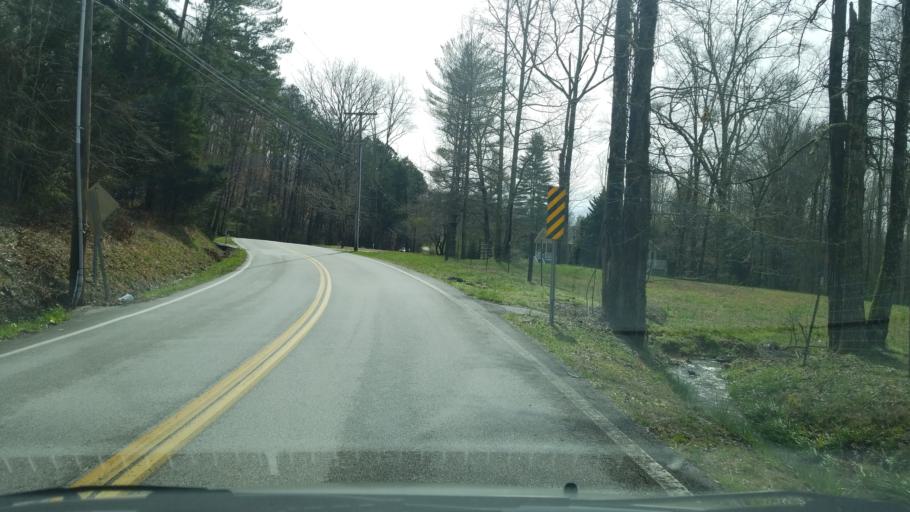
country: US
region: Tennessee
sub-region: Hamilton County
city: Harrison
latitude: 35.1335
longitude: -85.0838
